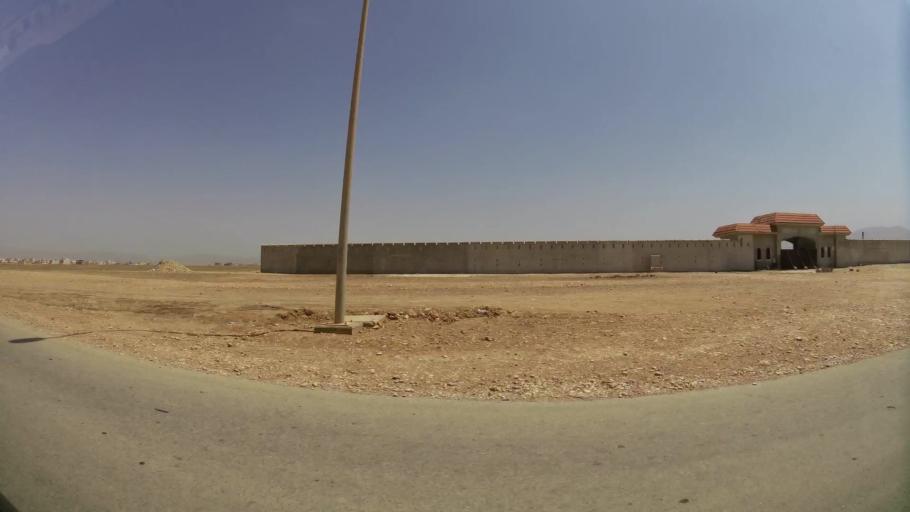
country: OM
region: Zufar
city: Salalah
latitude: 17.0563
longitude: 54.2028
